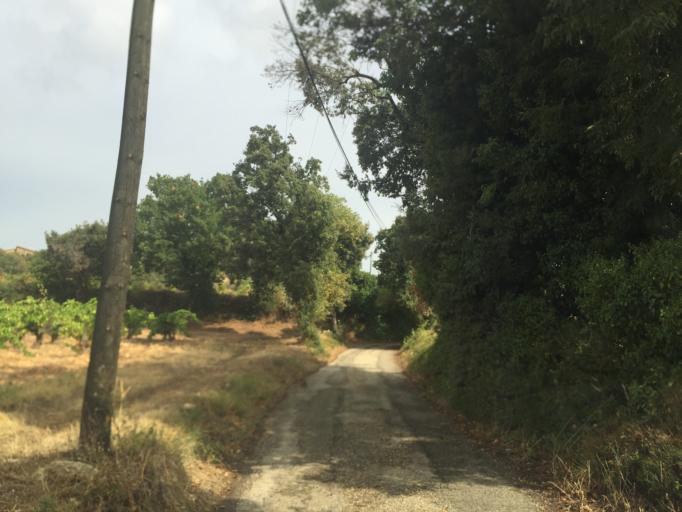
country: FR
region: Provence-Alpes-Cote d'Azur
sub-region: Departement du Vaucluse
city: Chateauneuf-du-Pape
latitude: 44.0607
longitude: 4.8362
